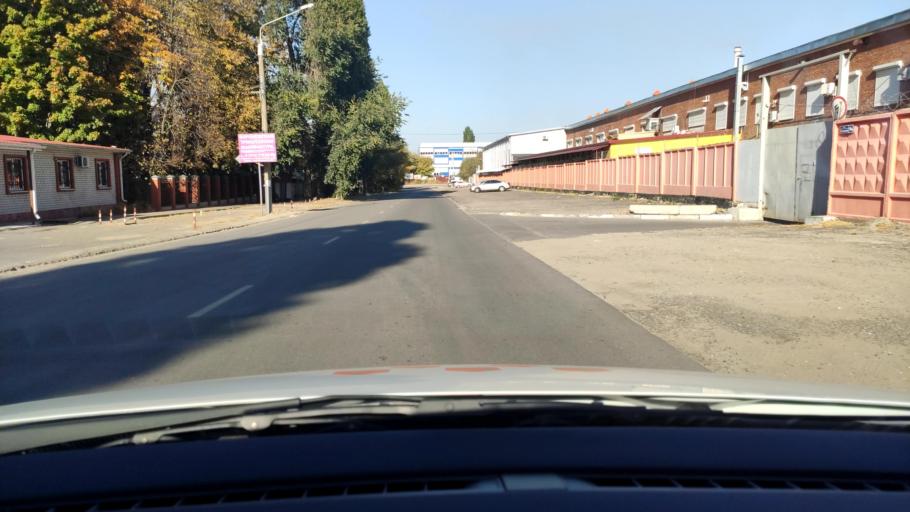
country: RU
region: Voronezj
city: Voronezh
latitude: 51.6800
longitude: 39.1462
